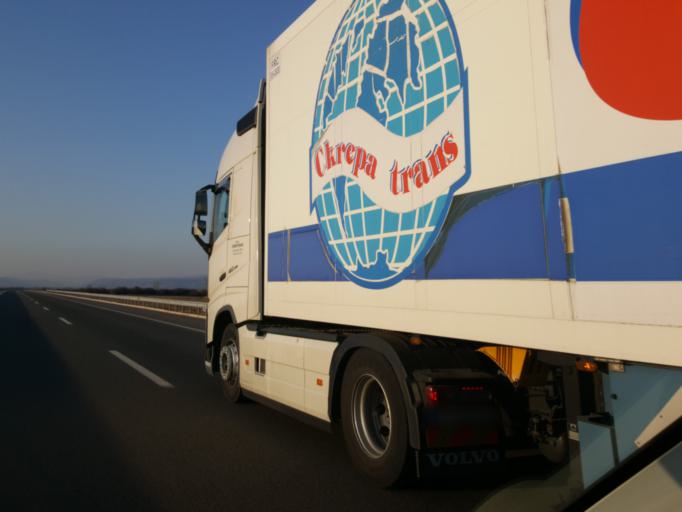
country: RS
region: Central Serbia
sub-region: Pirotski Okrug
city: Pirot
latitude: 43.0796
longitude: 22.6650
